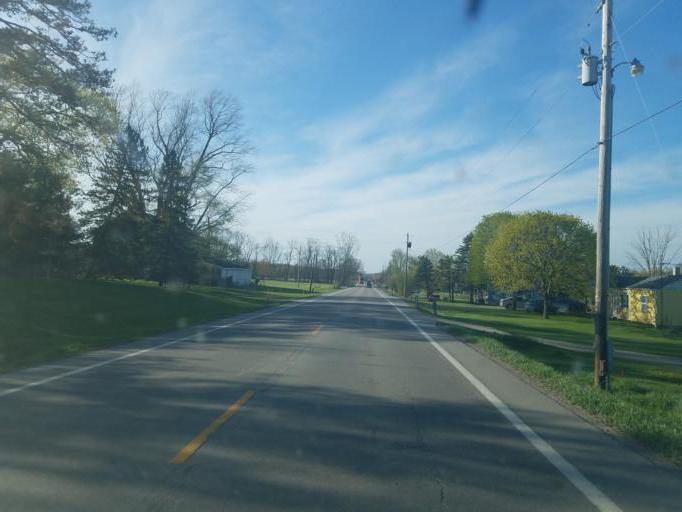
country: US
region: Ohio
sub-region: Ashland County
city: Ashland
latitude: 40.9339
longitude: -82.3526
